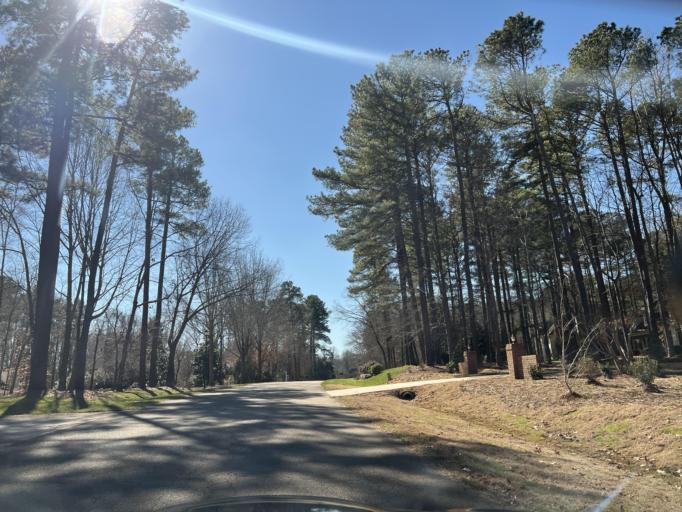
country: US
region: North Carolina
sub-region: Wake County
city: West Raleigh
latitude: 35.9058
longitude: -78.6170
